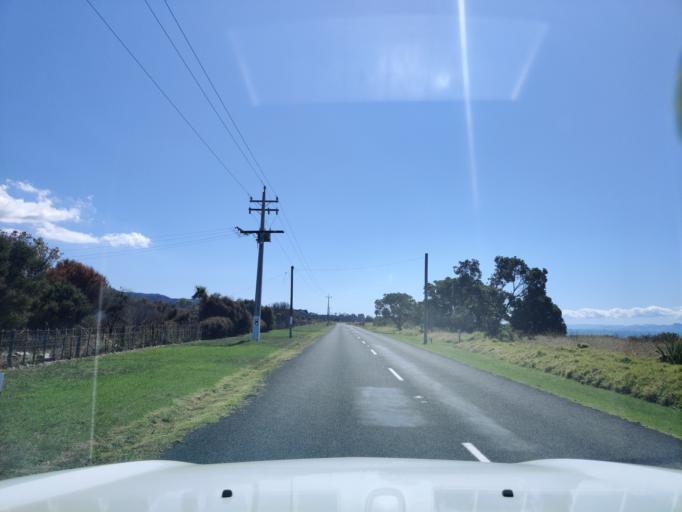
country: NZ
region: Waikato
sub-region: Thames-Coromandel District
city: Thames
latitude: -37.0730
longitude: 175.2959
